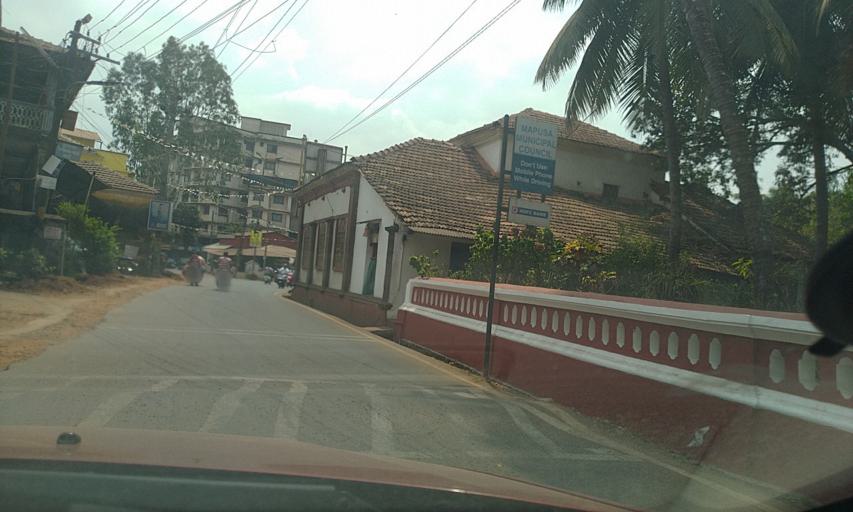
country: IN
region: Goa
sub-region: North Goa
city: Mapuca
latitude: 15.5924
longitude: 73.8064
